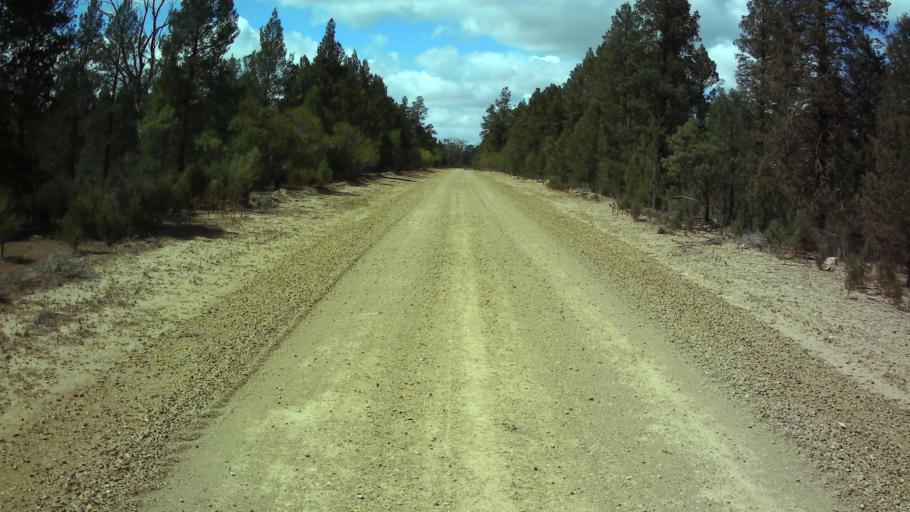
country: AU
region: New South Wales
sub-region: Weddin
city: Grenfell
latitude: -33.9124
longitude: 147.9205
